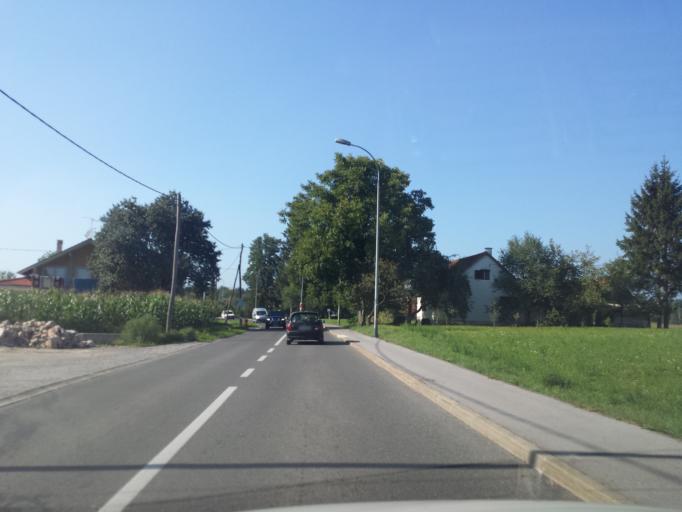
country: HR
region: Karlovacka
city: Ostarije
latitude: 45.2429
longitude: 15.2503
